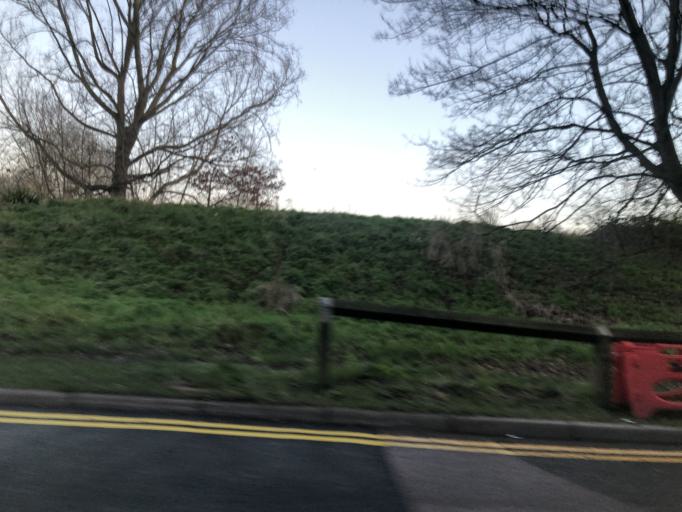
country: GB
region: England
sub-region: Greater London
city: Woolwich
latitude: 51.4741
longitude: 0.0474
